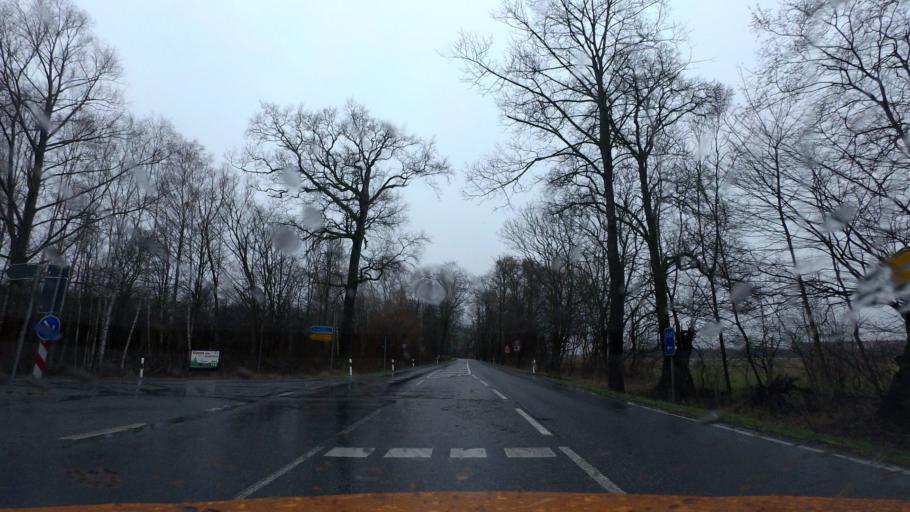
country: DE
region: Brandenburg
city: Brieselang
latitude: 52.5952
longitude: 13.0492
